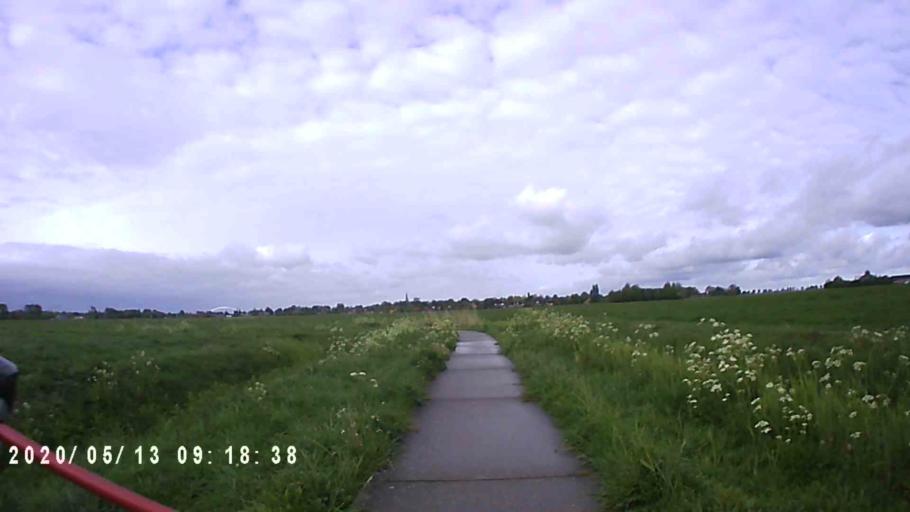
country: NL
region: Groningen
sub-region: Gemeente Zuidhorn
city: Noordhorn
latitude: 53.2659
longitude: 6.4109
